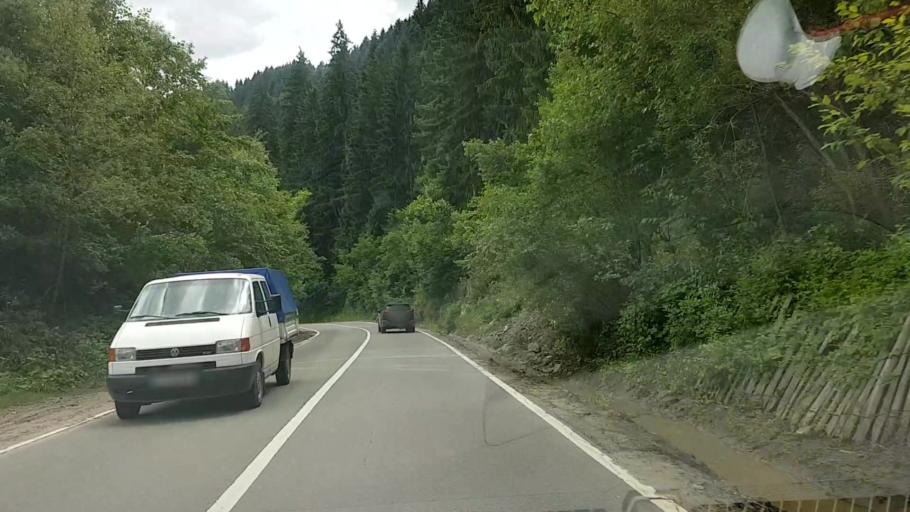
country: RO
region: Neamt
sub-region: Comuna Farcasa
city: Farcasa
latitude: 47.1397
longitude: 25.8597
